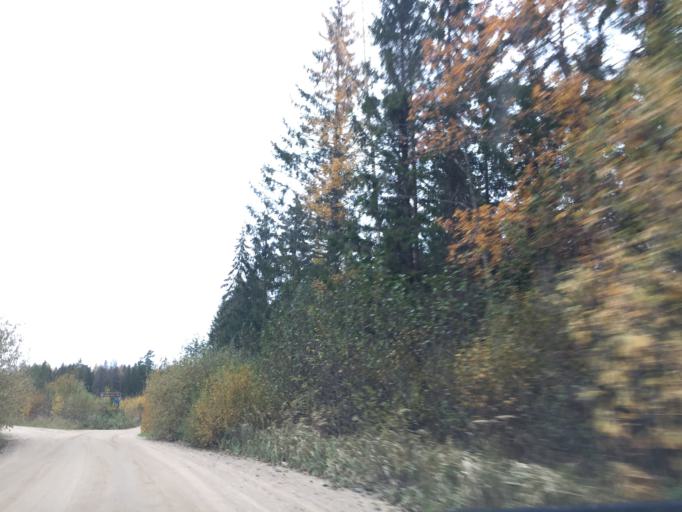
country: LV
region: Salacgrivas
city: Salacgriva
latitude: 57.5695
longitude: 24.4004
